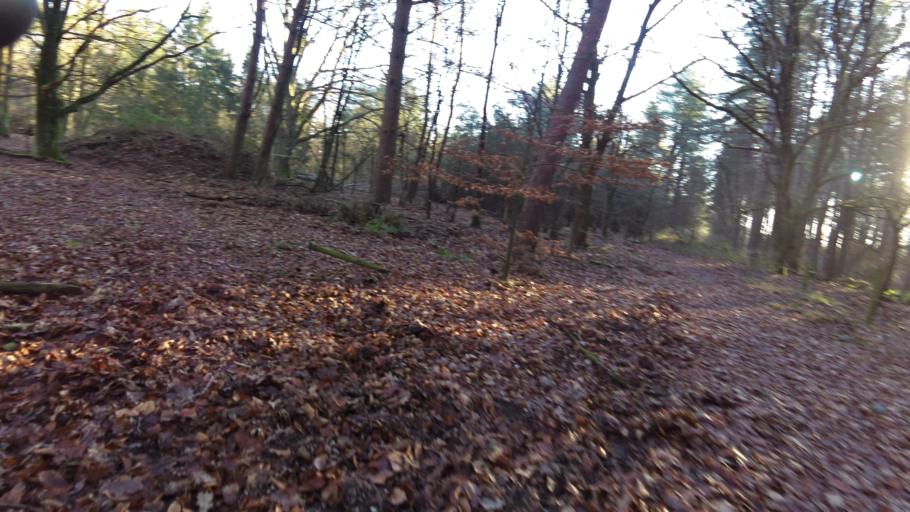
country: NL
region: Gelderland
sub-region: Gemeente Barneveld
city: Garderen
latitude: 52.2152
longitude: 5.7227
